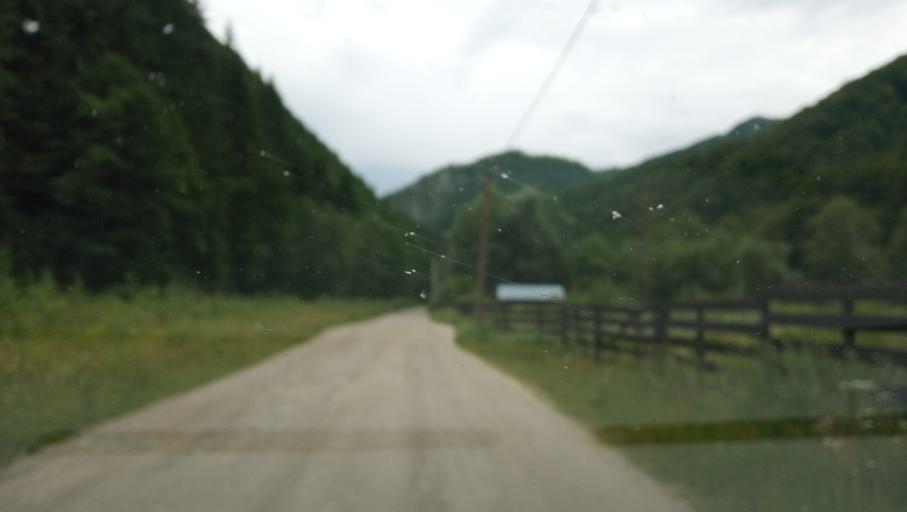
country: RO
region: Hunedoara
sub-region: Oras Petrila
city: Petrila
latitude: 45.4841
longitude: 23.4174
